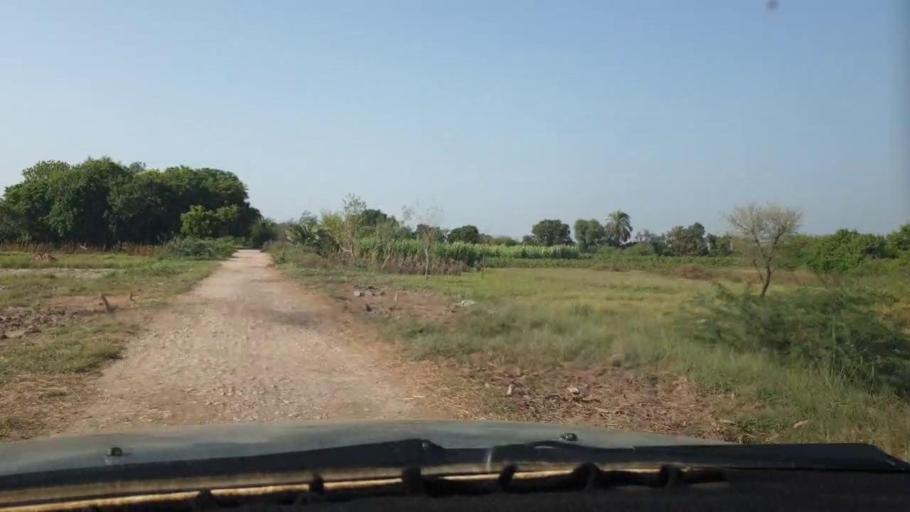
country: PK
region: Sindh
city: Chambar
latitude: 25.2673
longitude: 68.9237
